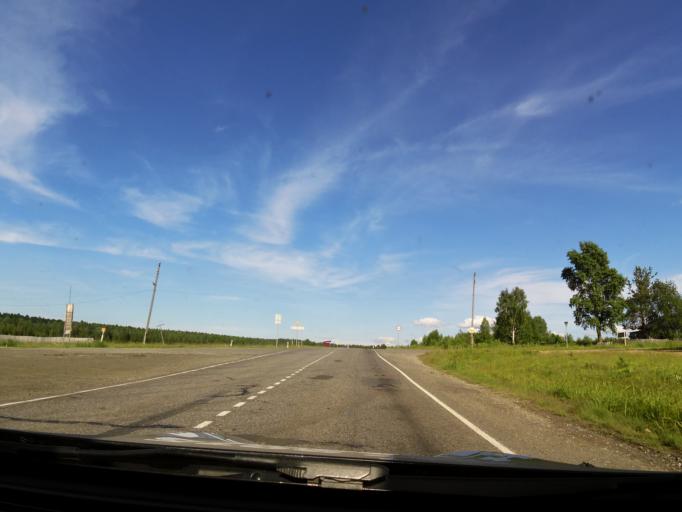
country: RU
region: Kirov
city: Chernaya Kholunitsa
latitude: 58.8586
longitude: 51.7047
